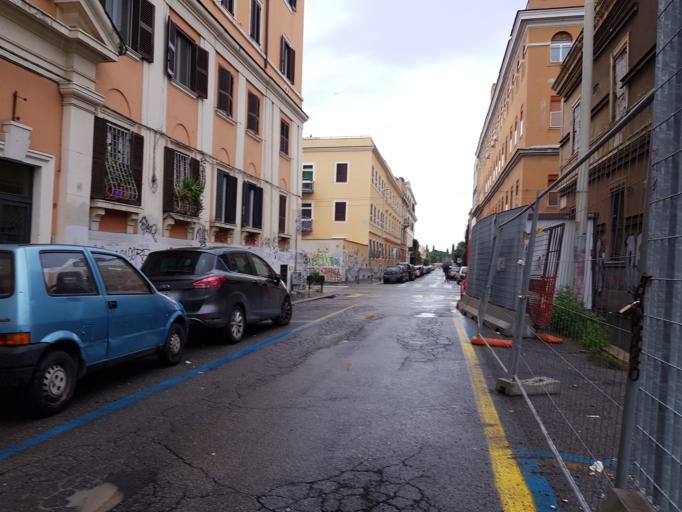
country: IT
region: Latium
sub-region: Citta metropolitana di Roma Capitale
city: Rome
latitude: 41.8986
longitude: 12.5180
